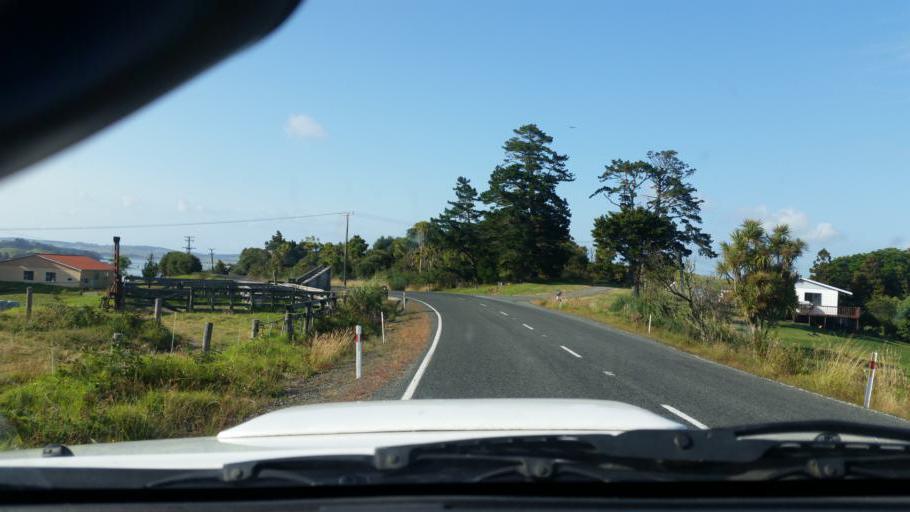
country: NZ
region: Northland
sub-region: Whangarei
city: Ruakaka
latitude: -36.1277
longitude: 174.2301
